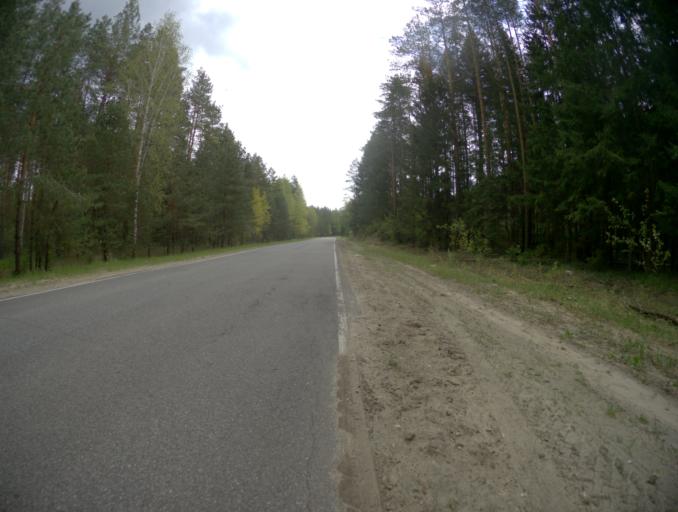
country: RU
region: Vladimir
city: Velikodvorskiy
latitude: 55.3943
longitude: 40.7139
